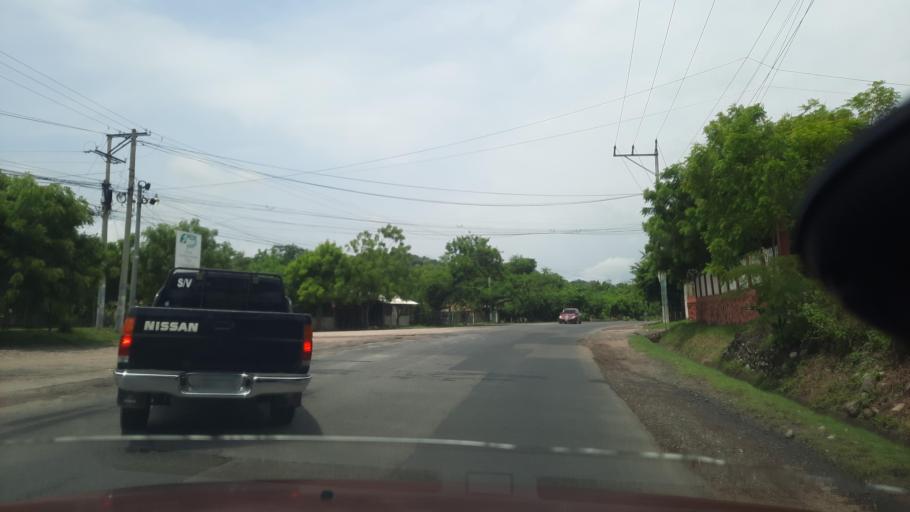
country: SV
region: La Union
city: Santa Rosa de Lima
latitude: 13.6193
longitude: -87.8560
